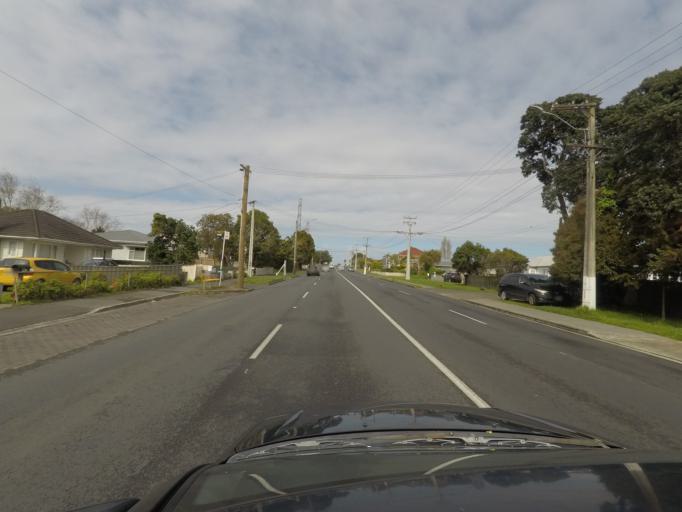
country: NZ
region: Auckland
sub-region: Auckland
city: Tamaki
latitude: -36.9054
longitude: 174.8407
